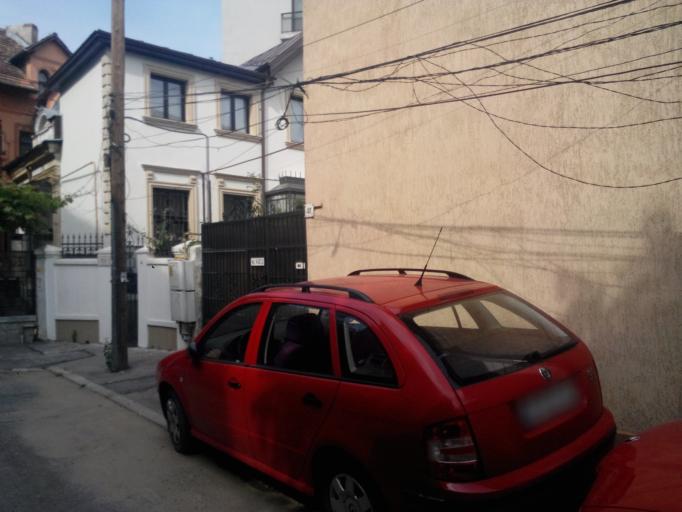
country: RO
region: Bucuresti
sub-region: Municipiul Bucuresti
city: Bucharest
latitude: 44.4419
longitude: 26.1193
